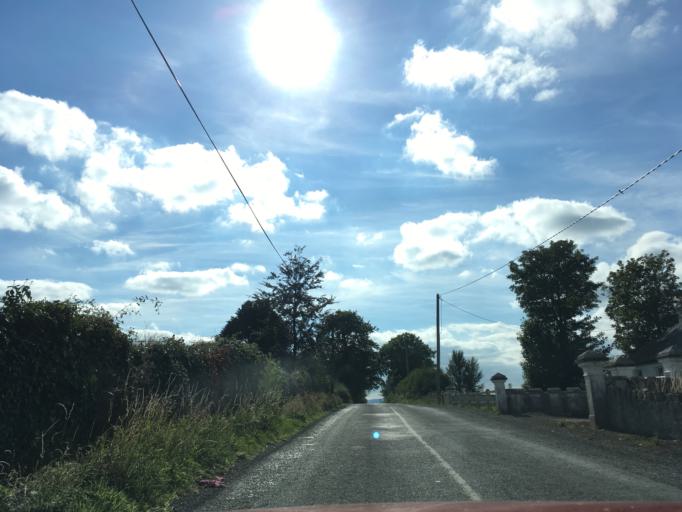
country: IE
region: Munster
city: Cashel
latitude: 52.4577
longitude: -7.9379
